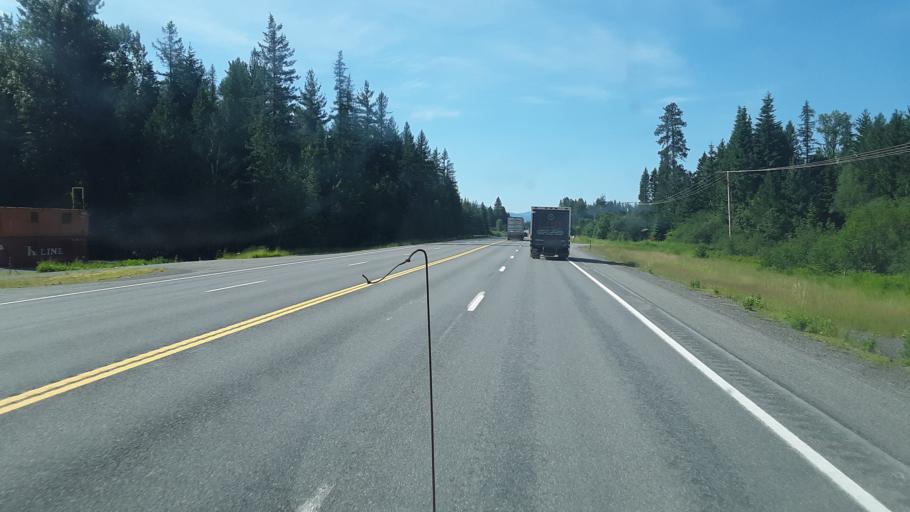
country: US
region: Idaho
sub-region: Bonner County
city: Ponderay
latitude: 48.3466
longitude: -116.5477
